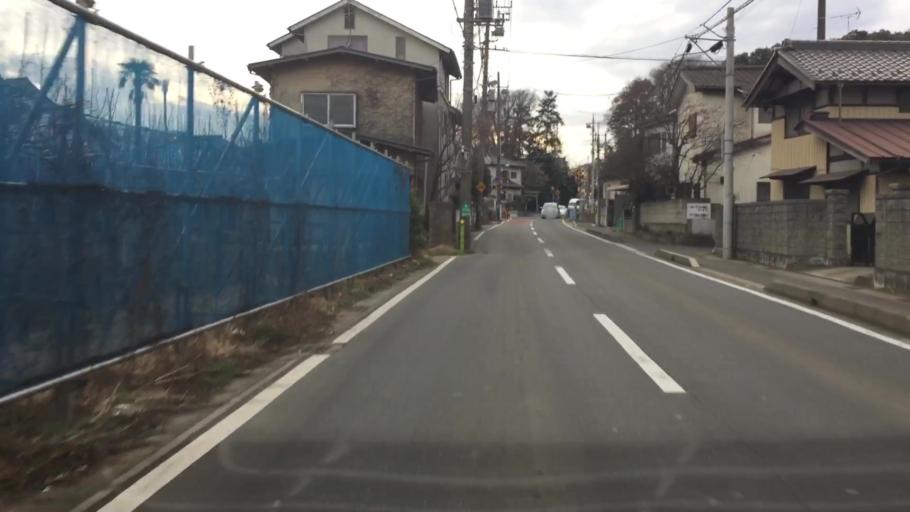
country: JP
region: Chiba
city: Shiroi
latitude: 35.7855
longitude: 140.0003
